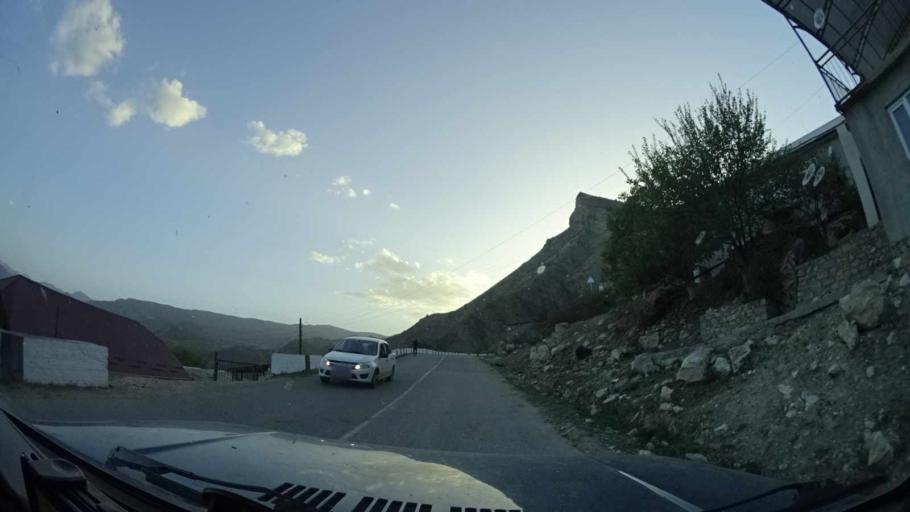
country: RU
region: Dagestan
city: Gunib
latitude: 42.3824
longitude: 46.9636
